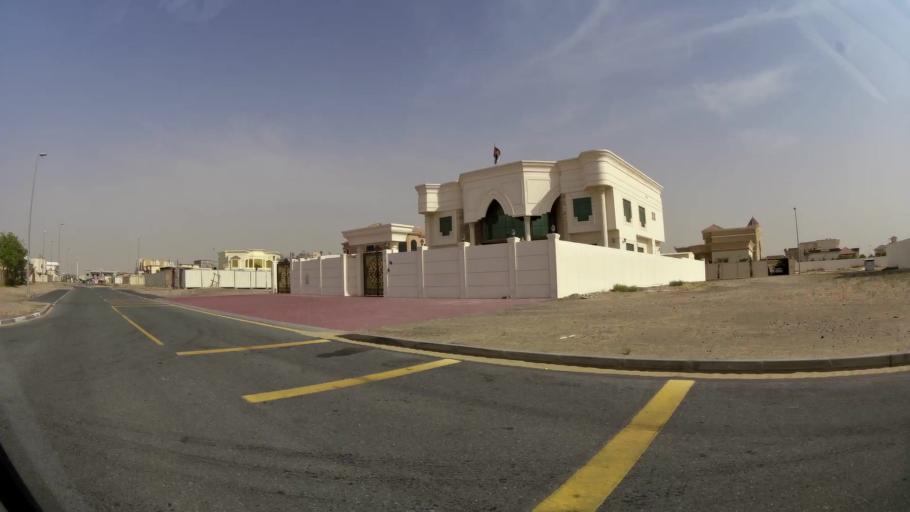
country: AE
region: Ash Shariqah
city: Sharjah
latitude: 25.2592
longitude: 55.4622
